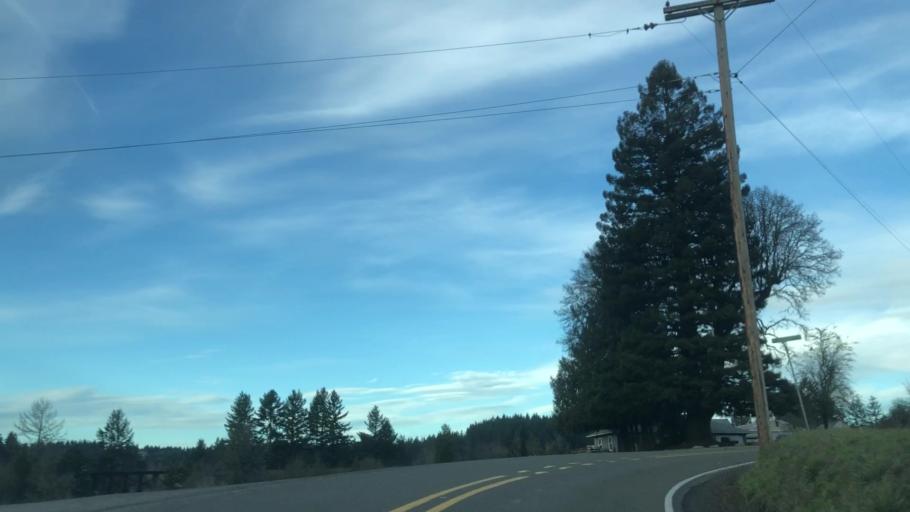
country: US
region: Oregon
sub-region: Washington County
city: Rockcreek
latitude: 45.5934
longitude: -122.9193
